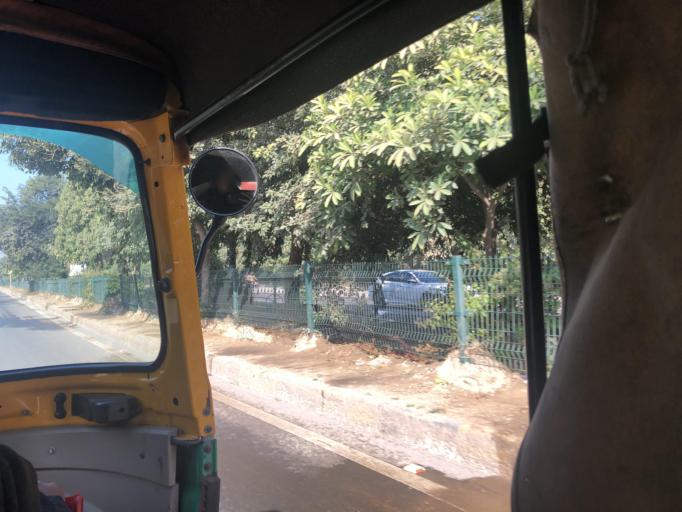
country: IN
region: Haryana
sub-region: Gurgaon
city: Gurgaon
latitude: 28.4426
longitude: 77.0846
